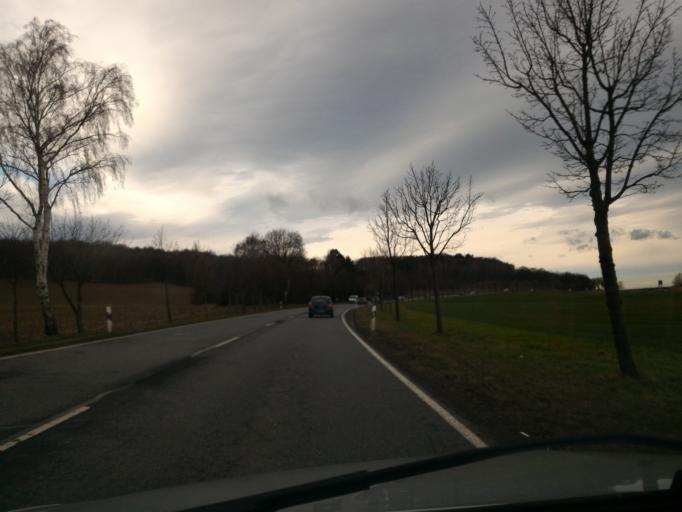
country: DE
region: Saxony
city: Radeberg
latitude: 51.0610
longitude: 13.9215
